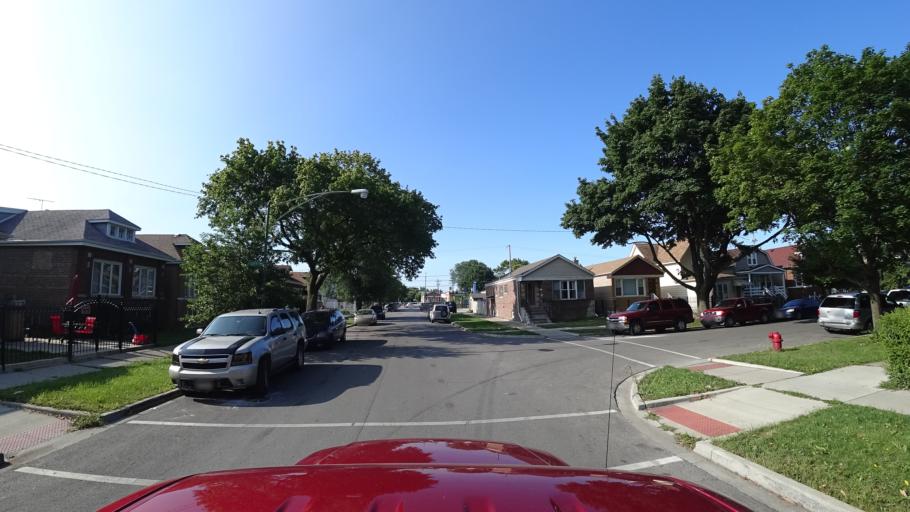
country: US
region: Illinois
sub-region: Cook County
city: Hometown
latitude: 41.7872
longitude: -87.7108
